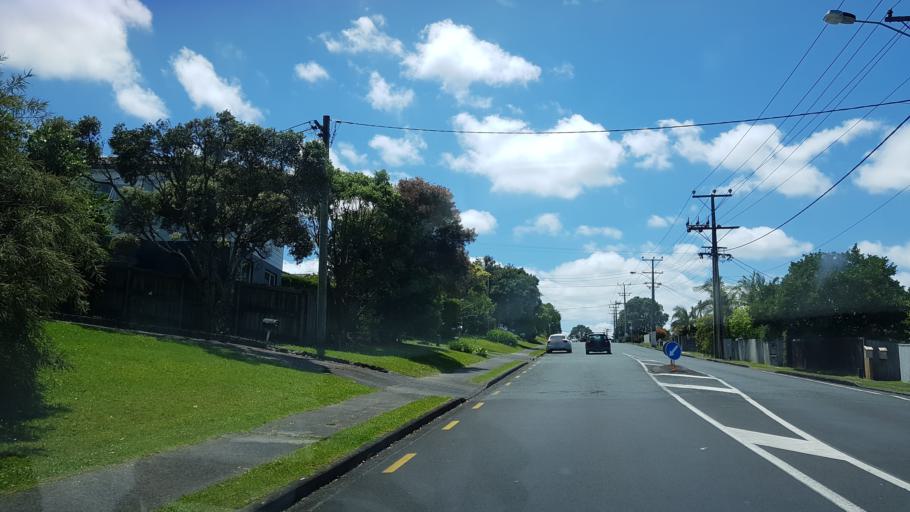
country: NZ
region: Auckland
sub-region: Auckland
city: North Shore
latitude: -36.7903
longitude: 174.7186
